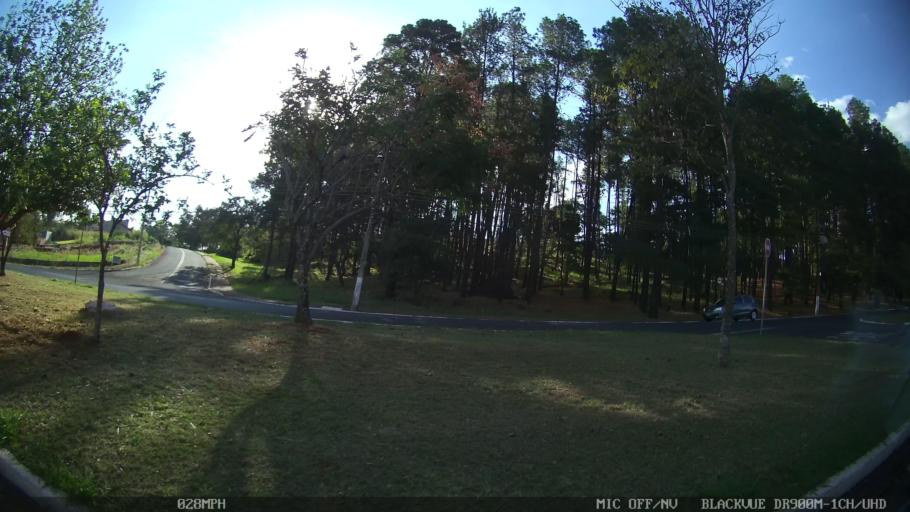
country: BR
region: Sao Paulo
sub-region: Ribeirao Preto
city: Ribeirao Preto
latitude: -21.2058
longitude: -47.7851
